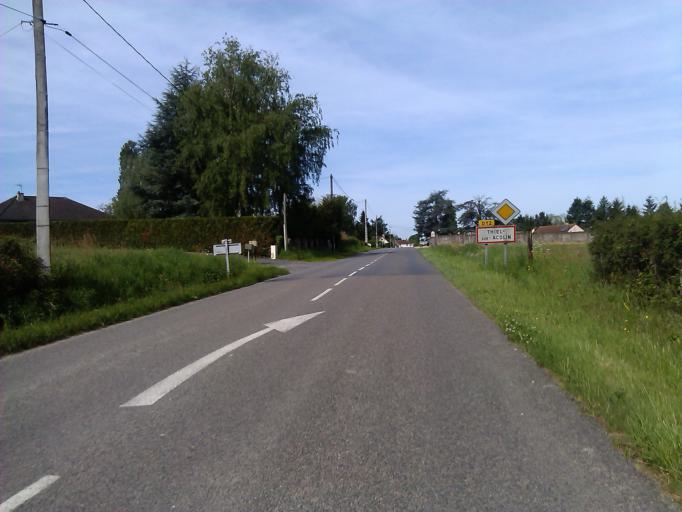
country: FR
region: Auvergne
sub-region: Departement de l'Allier
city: Dompierre-sur-Besbre
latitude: 46.5219
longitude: 3.5898
